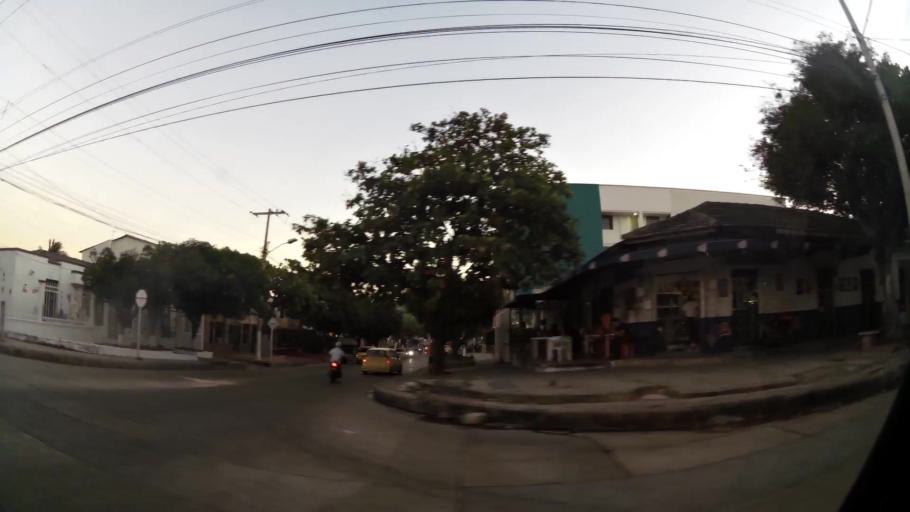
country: CO
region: Atlantico
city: Barranquilla
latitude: 10.9811
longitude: -74.8093
